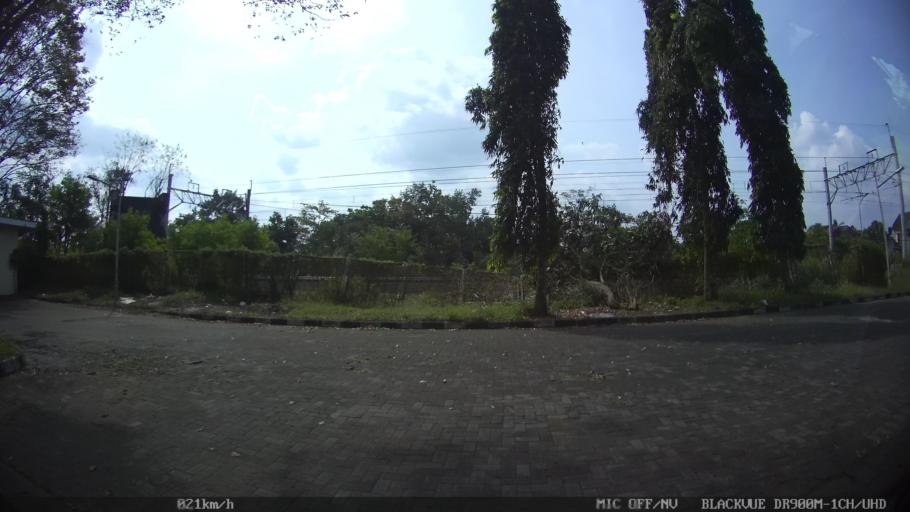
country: ID
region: Daerah Istimewa Yogyakarta
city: Depok
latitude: -7.7850
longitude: 110.4399
